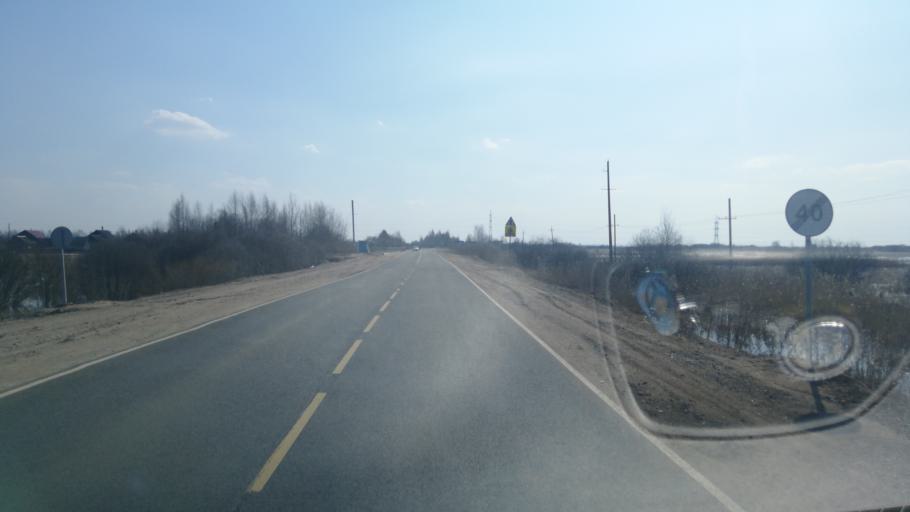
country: RU
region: Jaroslavl
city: Semibratovo
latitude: 57.2276
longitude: 39.5155
